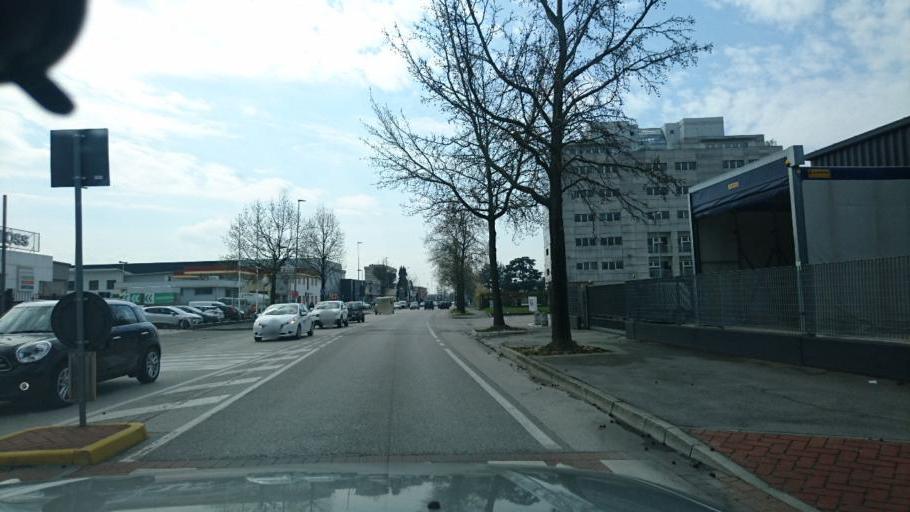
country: IT
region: Veneto
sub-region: Provincia di Padova
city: Noventa
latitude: 45.4004
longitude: 11.9288
